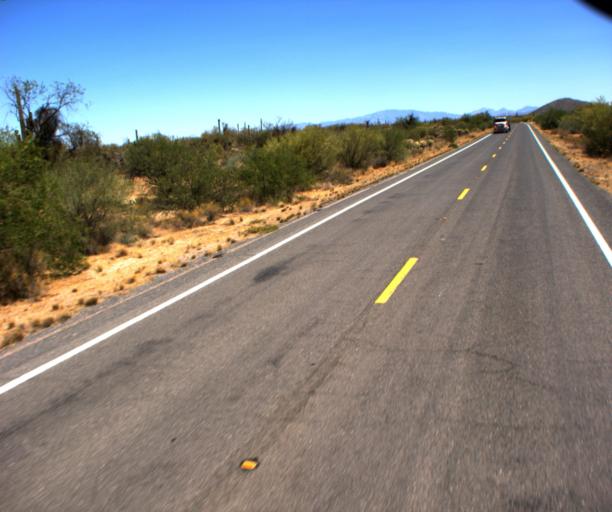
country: US
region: Arizona
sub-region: Pinal County
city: Florence
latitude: 32.7790
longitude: -111.1653
